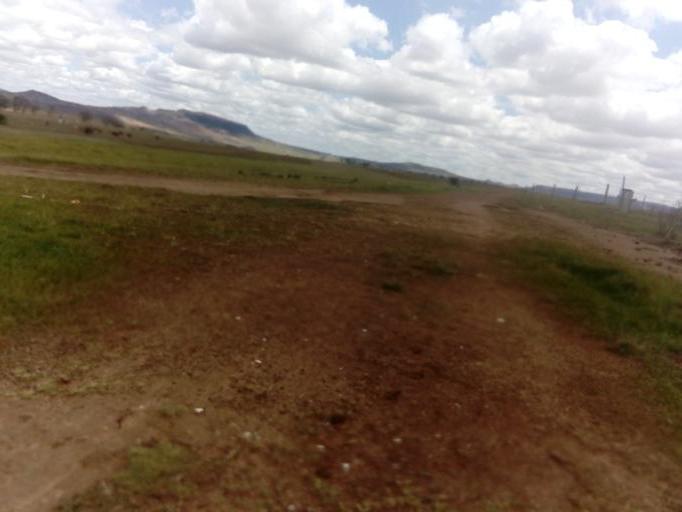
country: LS
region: Berea
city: Teyateyaneng
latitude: -29.1246
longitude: 27.7605
